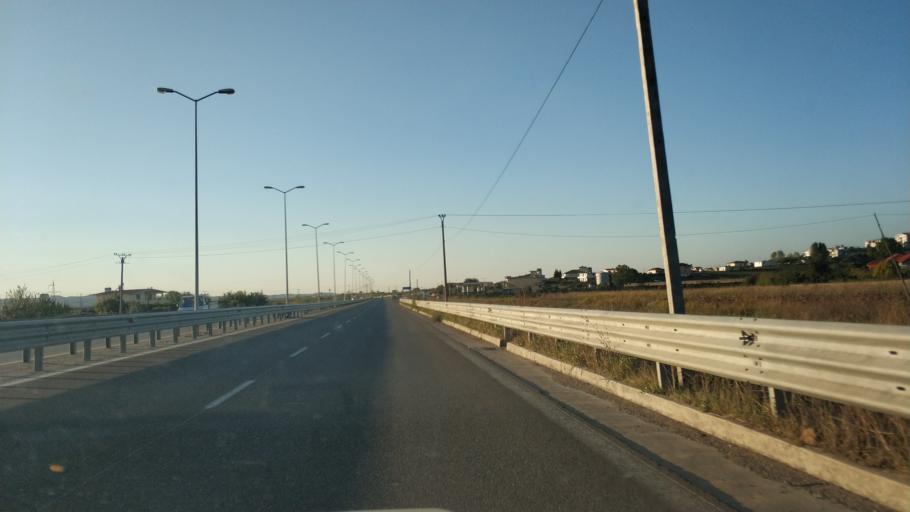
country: AL
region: Tirane
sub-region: Rrethi i Kavajes
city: Gose e Madhe
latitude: 41.0815
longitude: 19.6218
